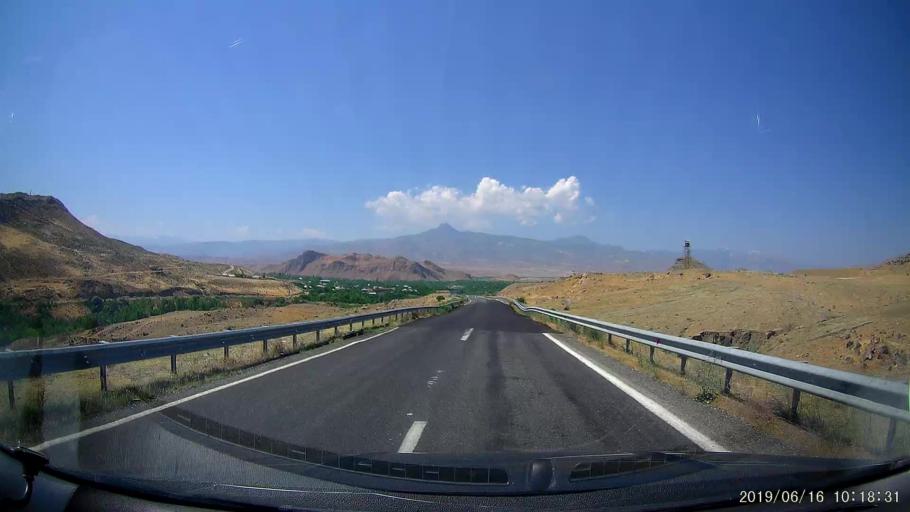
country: TR
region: Igdir
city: Tuzluca
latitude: 40.1596
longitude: 43.6670
